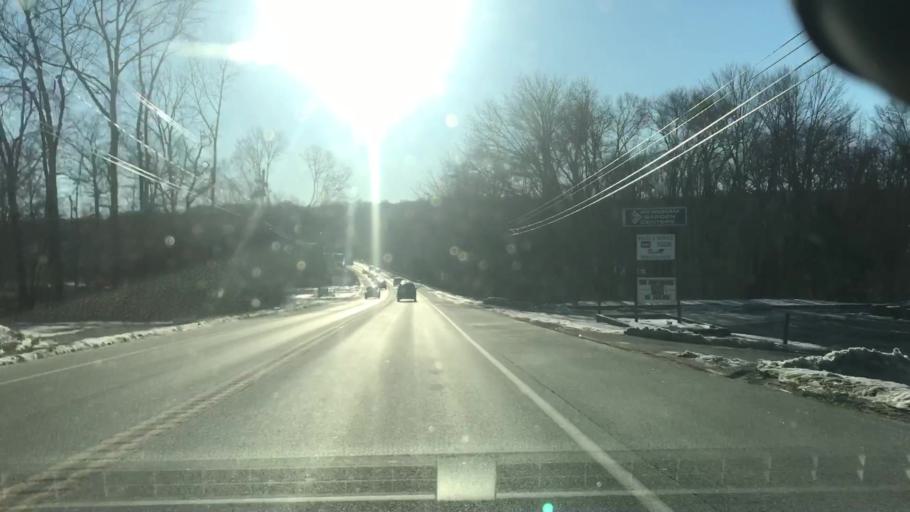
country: US
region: New Jersey
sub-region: Morris County
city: Chester
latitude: 40.8005
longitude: -74.7116
